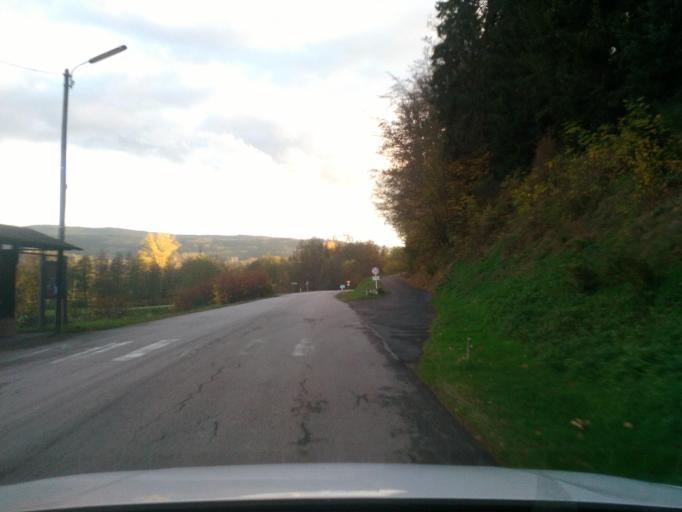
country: FR
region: Lorraine
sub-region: Departement des Vosges
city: Ban-de-Laveline
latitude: 48.3000
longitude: 7.0717
